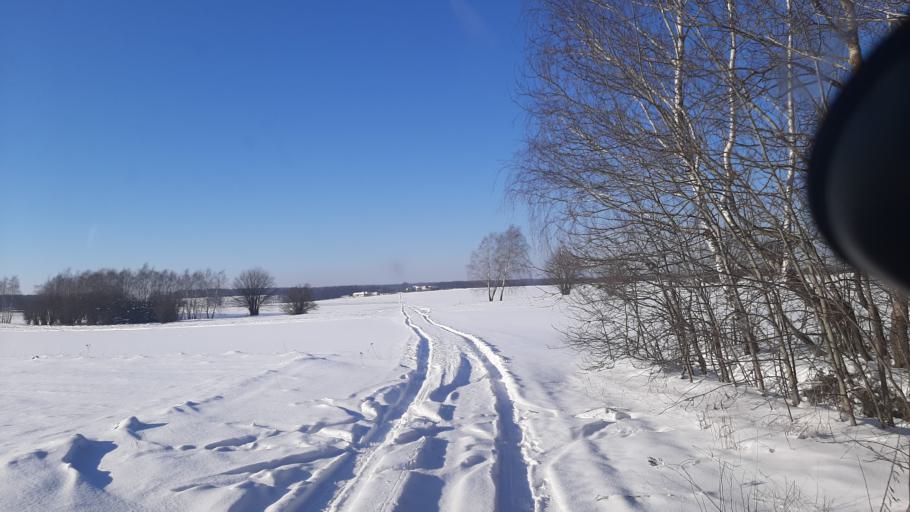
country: PL
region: Lublin Voivodeship
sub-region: Powiat lubelski
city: Jastkow
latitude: 51.3787
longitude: 22.4333
